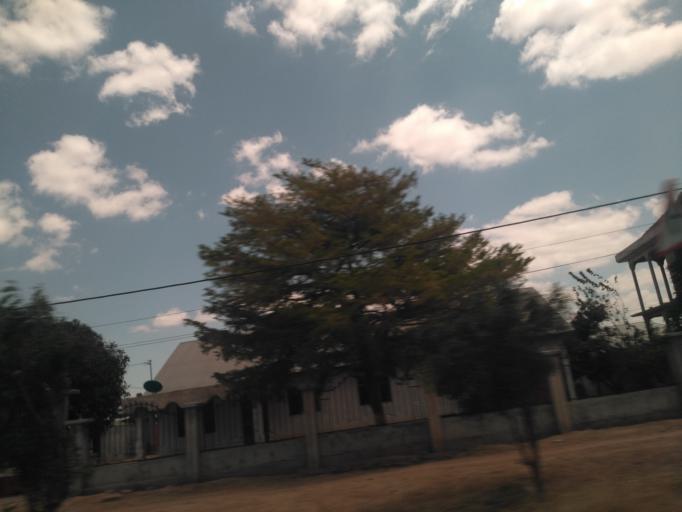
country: TZ
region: Dodoma
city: Kisasa
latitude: -6.1779
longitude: 35.7875
